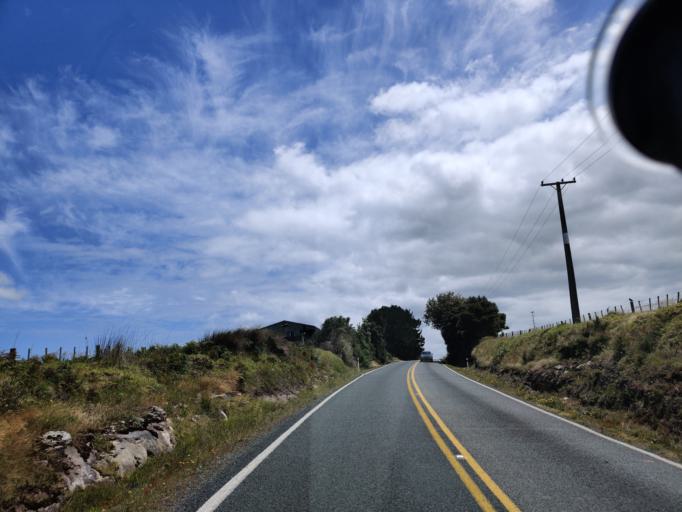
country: NZ
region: Northland
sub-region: Far North District
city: Kaitaia
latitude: -34.7068
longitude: 173.0324
